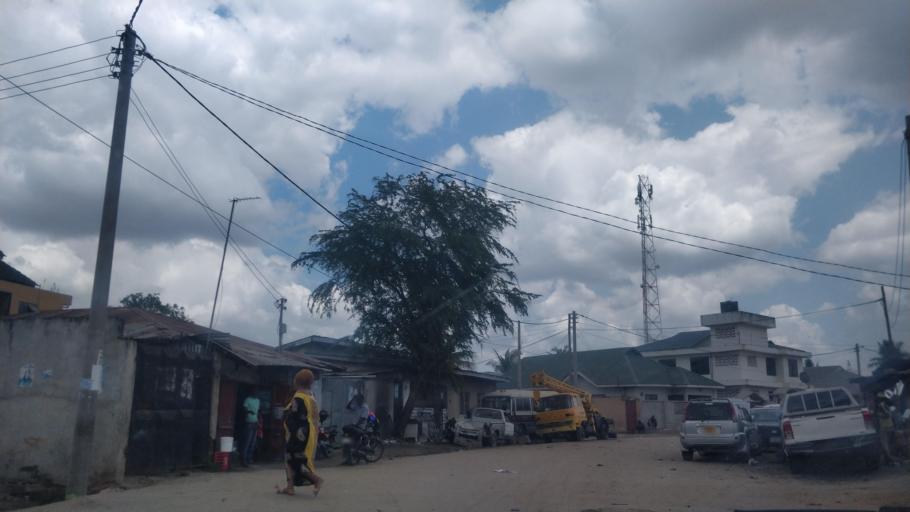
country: TZ
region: Dar es Salaam
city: Magomeni
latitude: -6.8120
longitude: 39.2567
